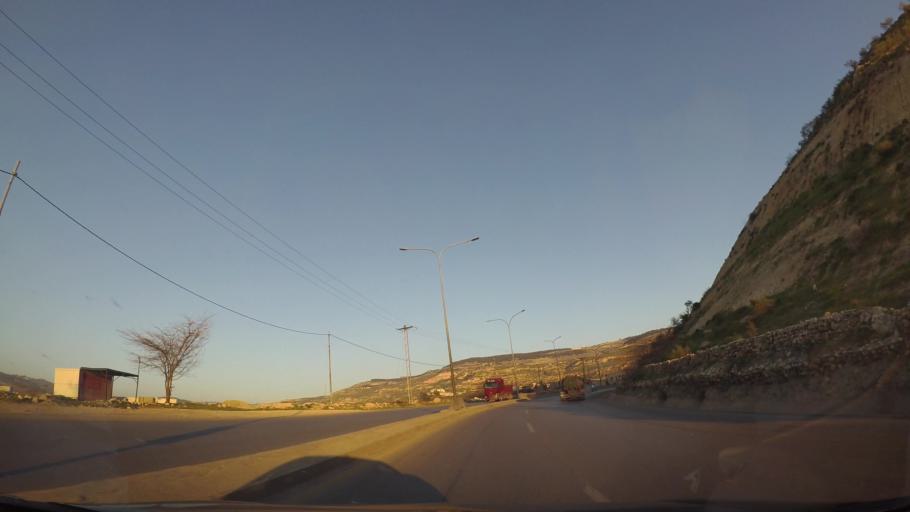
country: JO
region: Amman
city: Umm as Summaq
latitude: 31.8686
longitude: 35.7471
